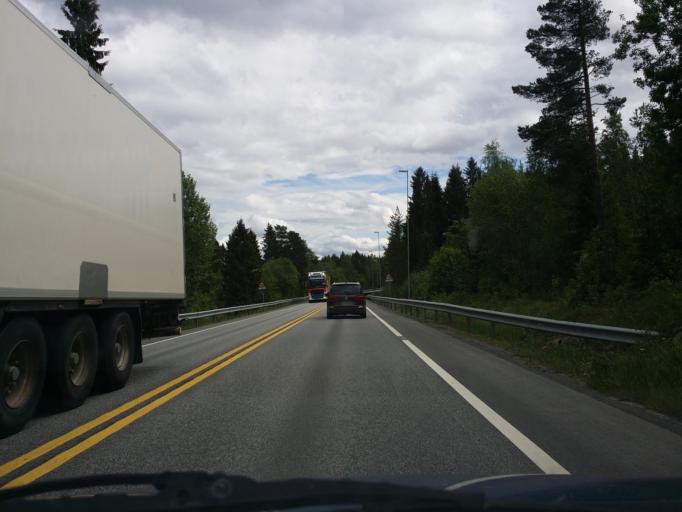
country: NO
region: Hedmark
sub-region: Stange
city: Stange
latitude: 60.7180
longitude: 11.2421
